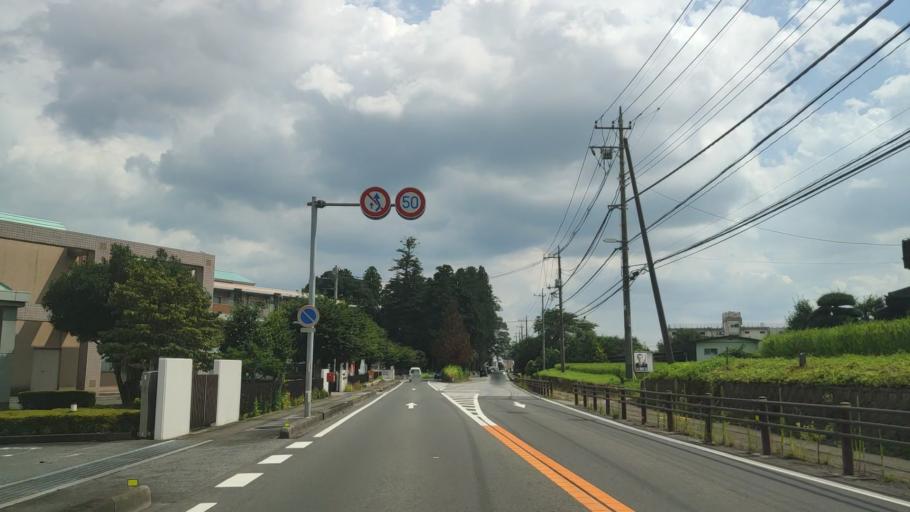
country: JP
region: Tochigi
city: Utsunomiya-shi
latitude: 36.6585
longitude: 139.8396
